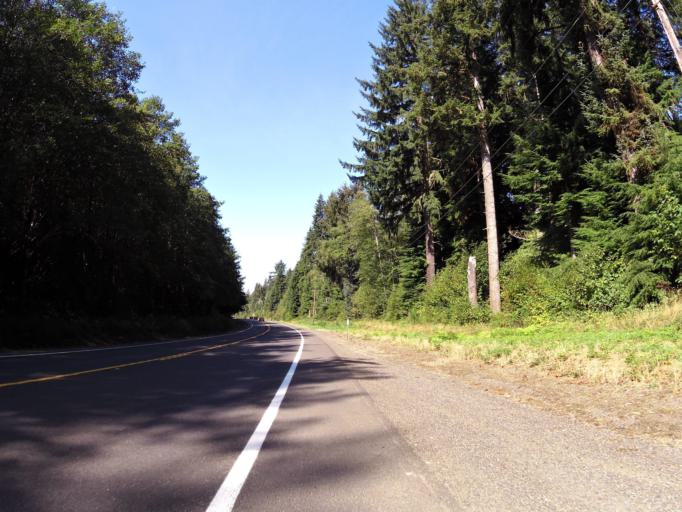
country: US
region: Washington
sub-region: Wahkiakum County
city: Cathlamet
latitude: 46.1720
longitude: -123.4905
